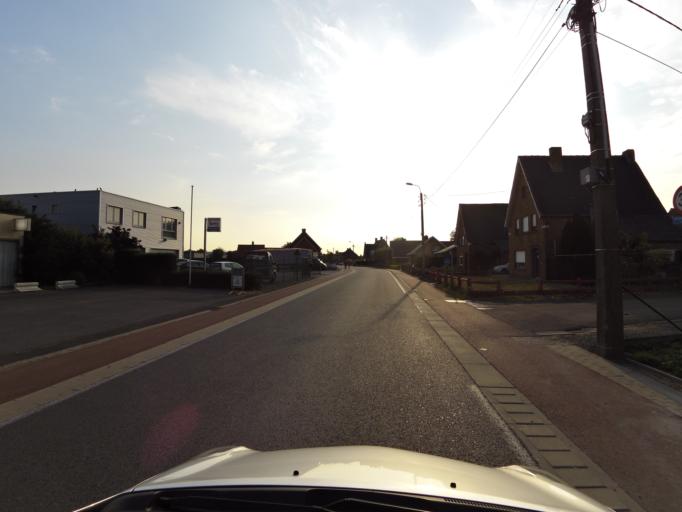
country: BE
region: Flanders
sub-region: Provincie West-Vlaanderen
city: Torhout
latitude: 51.0822
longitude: 3.1103
